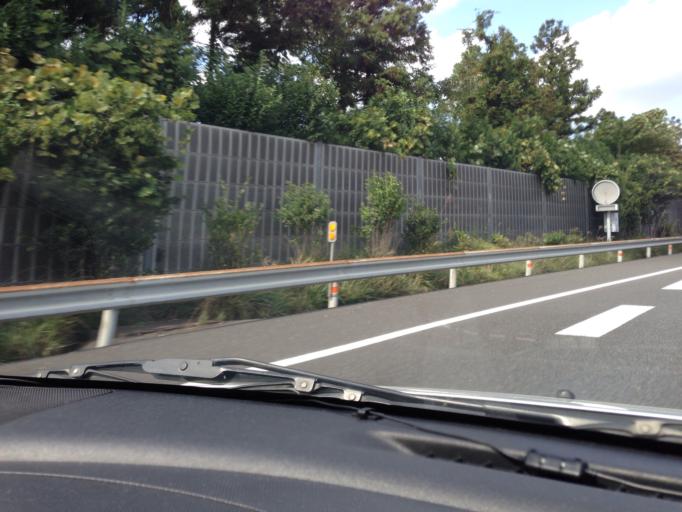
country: JP
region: Ibaraki
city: Mito-shi
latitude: 36.3852
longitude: 140.3865
